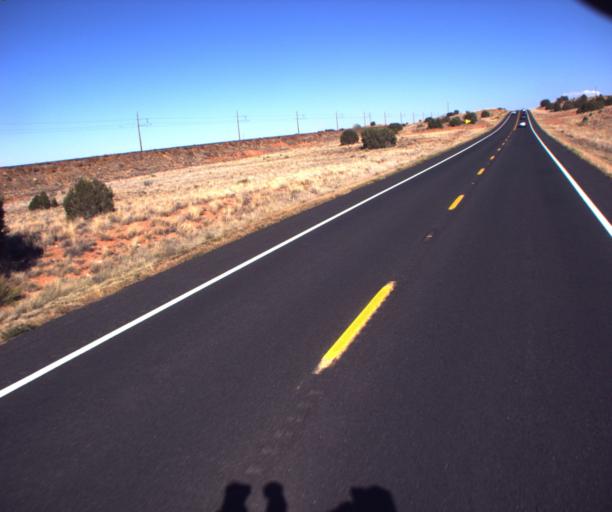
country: US
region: Arizona
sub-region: Coconino County
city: Kaibito
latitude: 36.4076
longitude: -110.8361
